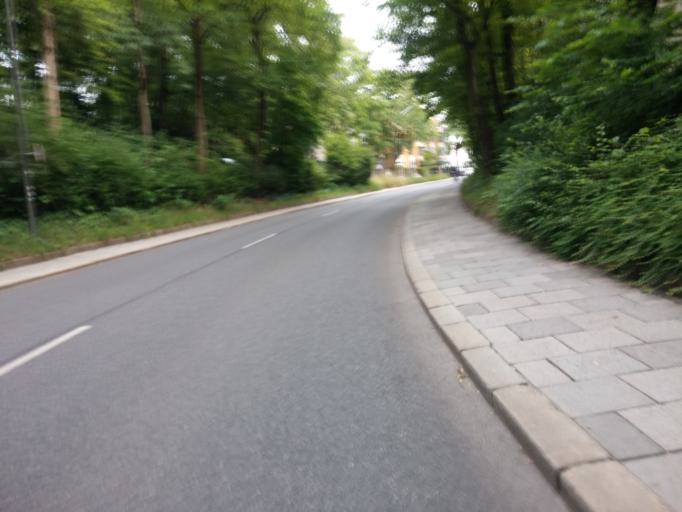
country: DE
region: Bavaria
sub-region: Upper Bavaria
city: Bogenhausen
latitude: 48.1482
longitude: 11.6028
